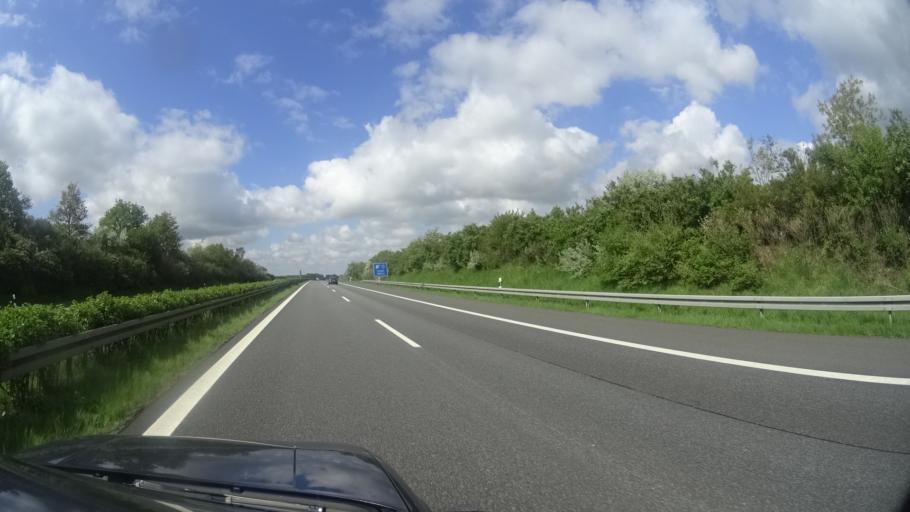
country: DE
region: Mecklenburg-Vorpommern
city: Laage
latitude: 53.8724
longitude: 12.2590
